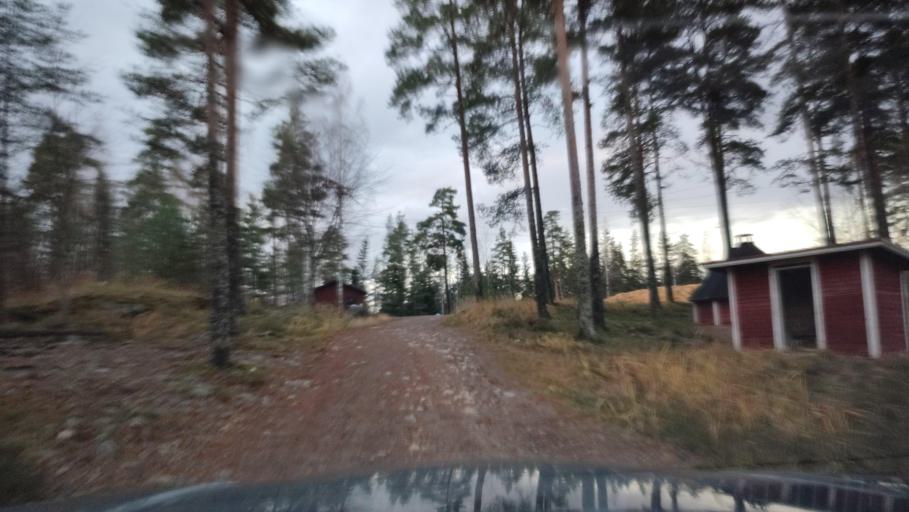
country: FI
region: Southern Ostrobothnia
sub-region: Suupohja
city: Karijoki
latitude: 62.2819
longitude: 21.6292
